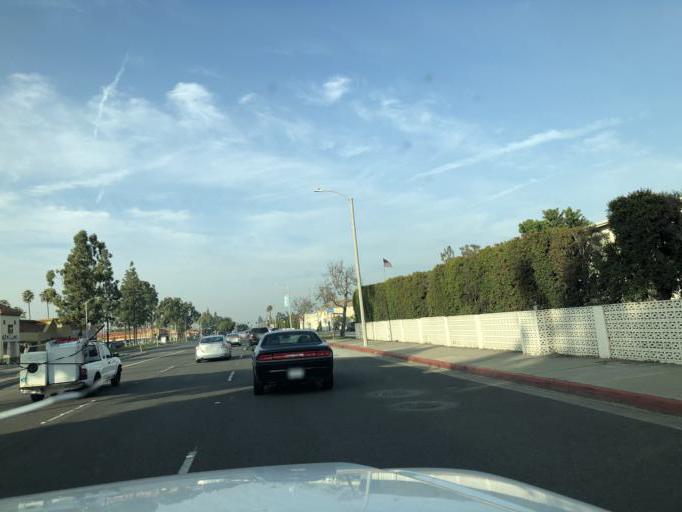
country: US
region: California
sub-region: Orange County
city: Fountain Valley
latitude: 33.6913
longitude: -117.9541
